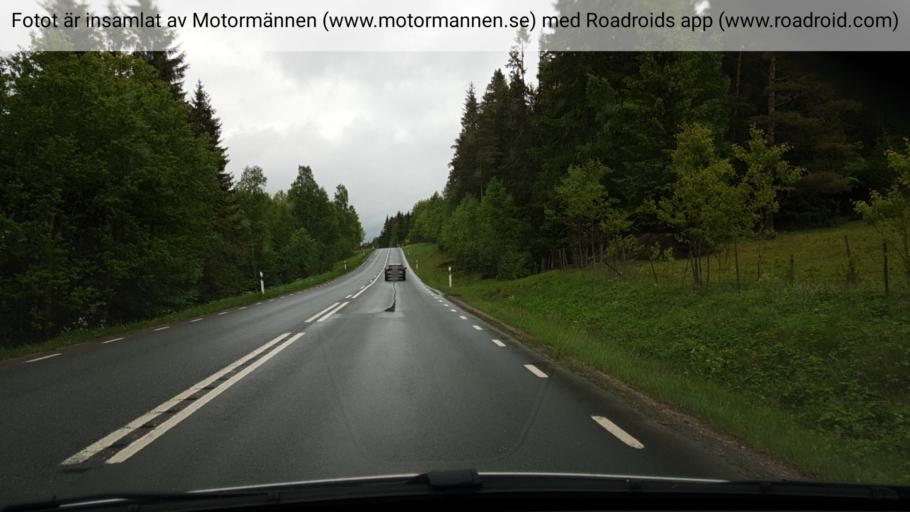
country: SE
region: Joenkoeping
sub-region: Aneby Kommun
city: Aneby
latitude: 57.8943
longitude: 14.8868
